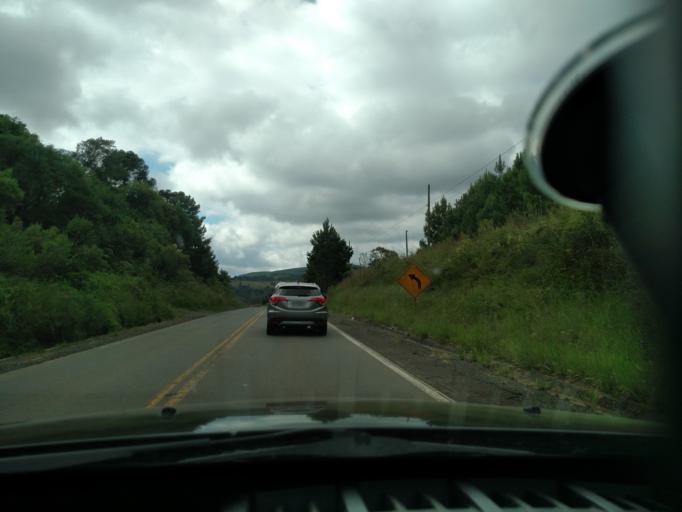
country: BR
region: Santa Catarina
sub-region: Lages
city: Lages
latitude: -27.8634
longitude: -50.2106
